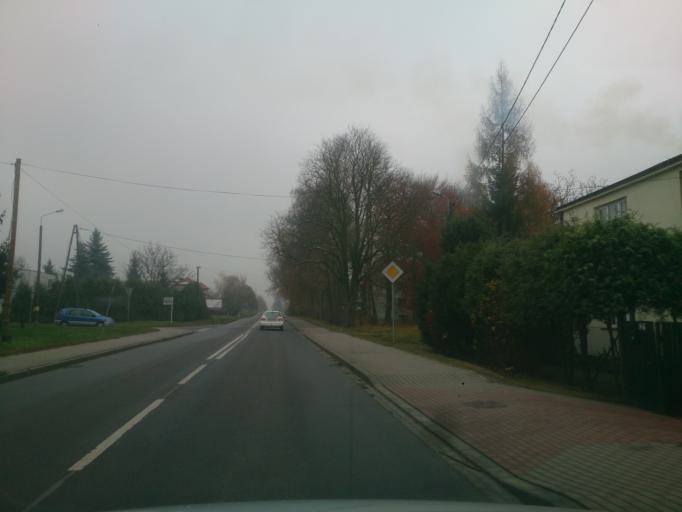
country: PL
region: Kujawsko-Pomorskie
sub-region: Powiat rypinski
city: Rypin
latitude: 53.0584
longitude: 19.4202
